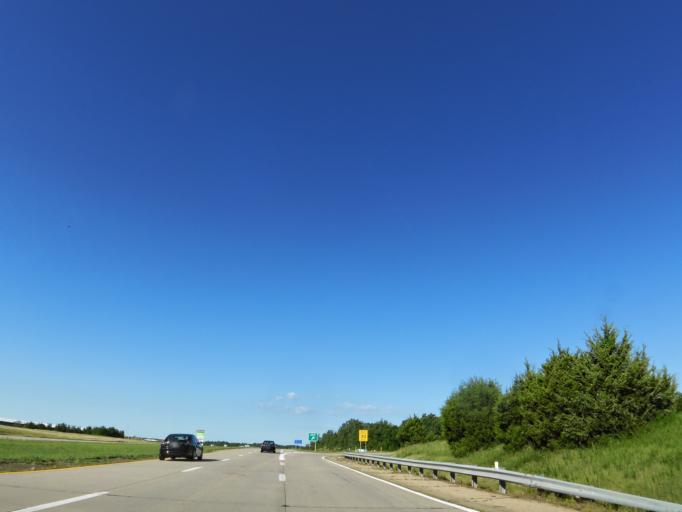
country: US
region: Missouri
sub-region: Butler County
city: Poplar Bluff
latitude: 36.7945
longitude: -90.4437
